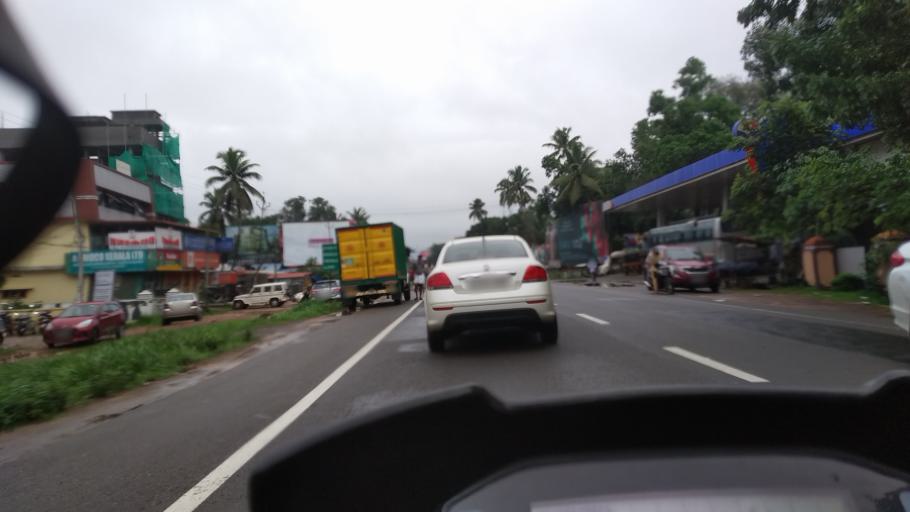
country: IN
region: Kerala
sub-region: Alappuzha
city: Mavelikara
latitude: 9.2757
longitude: 76.4598
